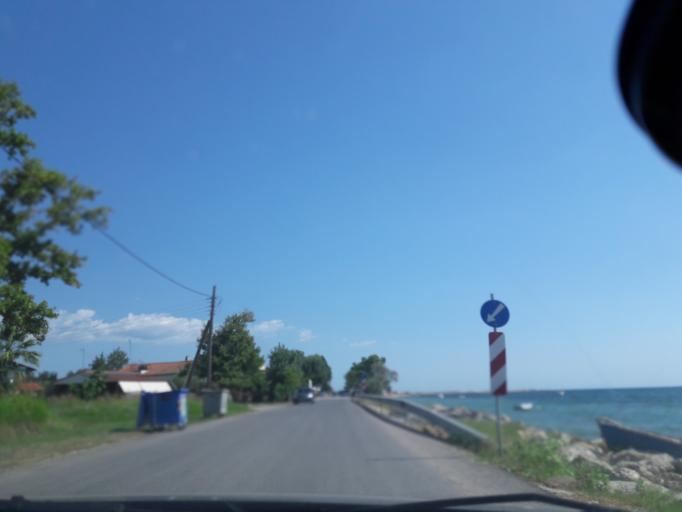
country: GR
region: Central Macedonia
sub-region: Nomos Chalkidikis
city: Nea Kallikrateia
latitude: 40.3417
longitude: 23.0162
